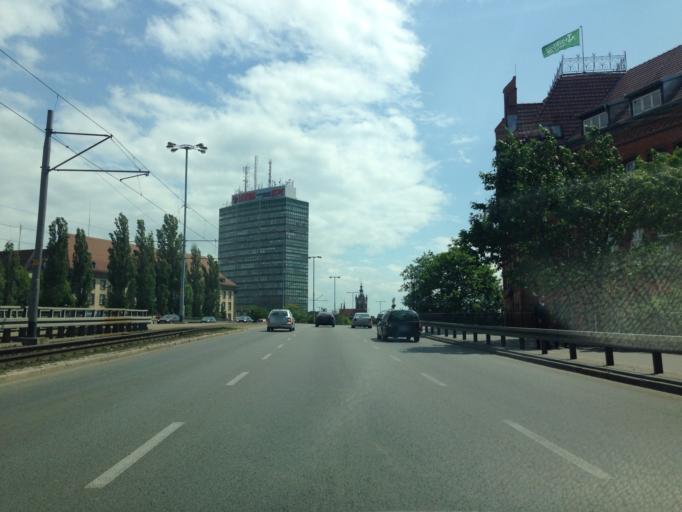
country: PL
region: Pomeranian Voivodeship
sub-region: Gdansk
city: Gdansk
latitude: 54.3605
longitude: 18.6431
